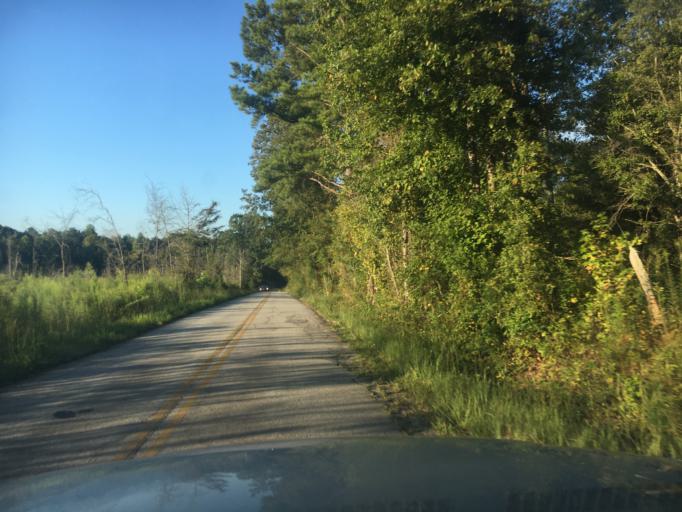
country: US
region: South Carolina
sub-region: Spartanburg County
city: Woodruff
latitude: 34.6839
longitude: -81.9597
